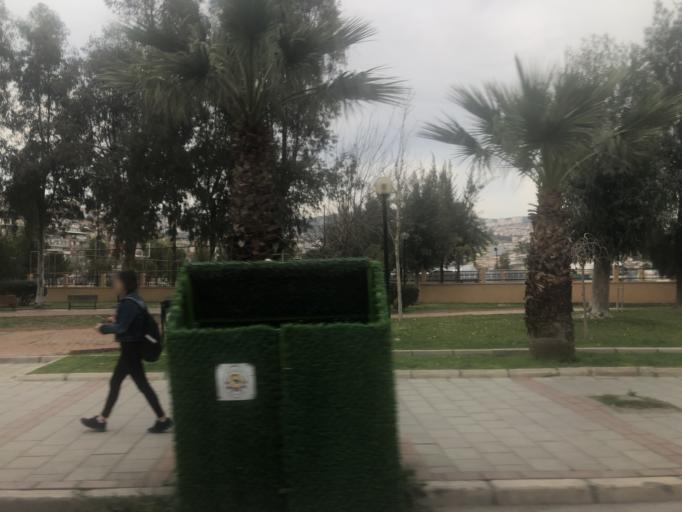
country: TR
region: Izmir
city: Karsiyaka
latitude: 38.4896
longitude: 27.0695
